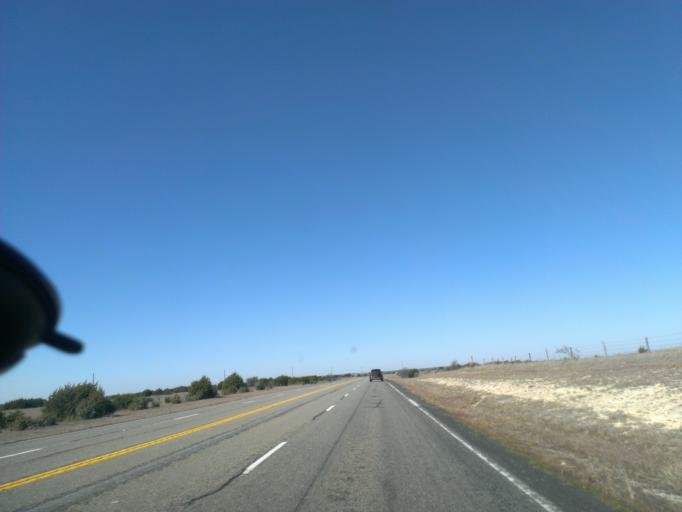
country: US
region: Texas
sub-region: Burnet County
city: Bertram
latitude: 30.8998
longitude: -97.9662
